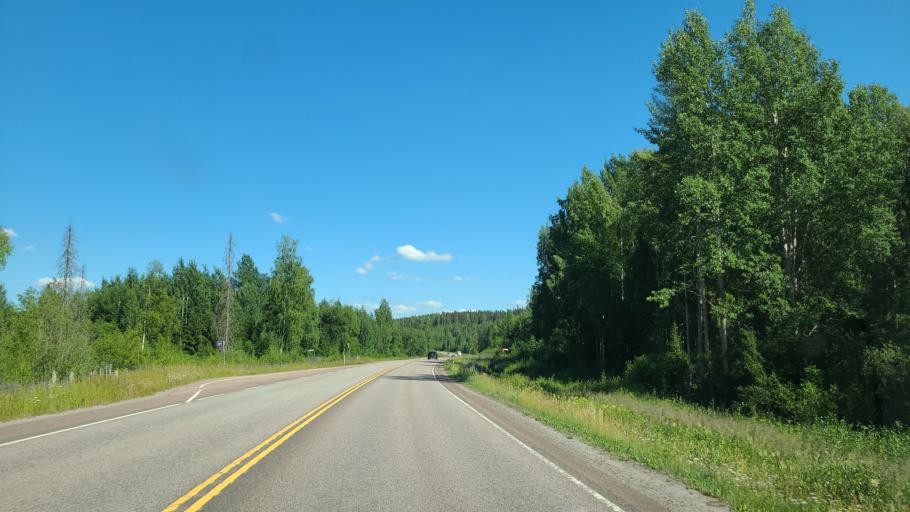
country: FI
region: Central Finland
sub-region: Jyvaeskylae
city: Petaejaevesi
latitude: 62.2734
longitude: 25.3627
